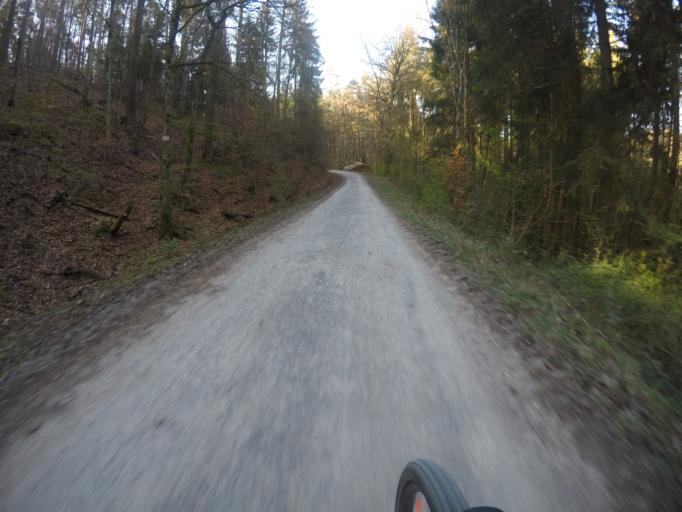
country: DE
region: Baden-Wuerttemberg
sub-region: Regierungsbezirk Stuttgart
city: Schlaitdorf
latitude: 48.6148
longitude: 9.2043
